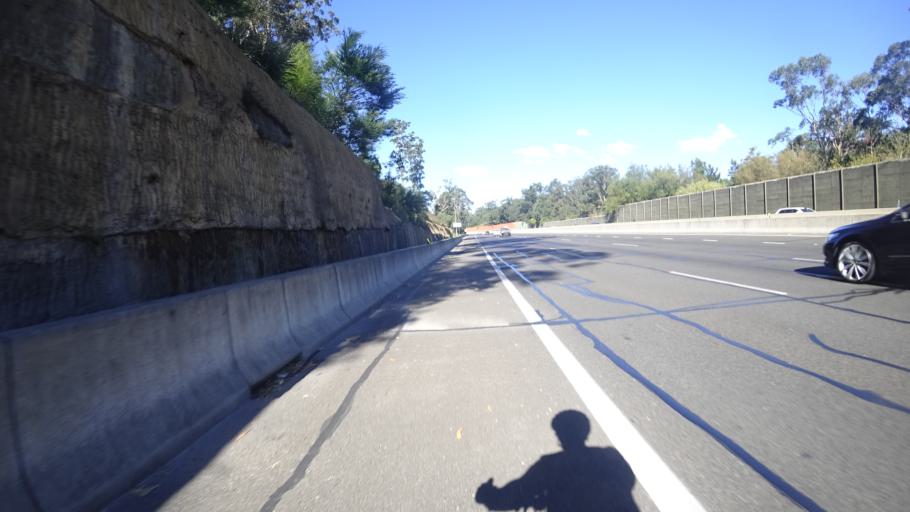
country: AU
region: New South Wales
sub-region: Hornsby Shire
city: Beecroft
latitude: -33.7590
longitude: 151.0666
